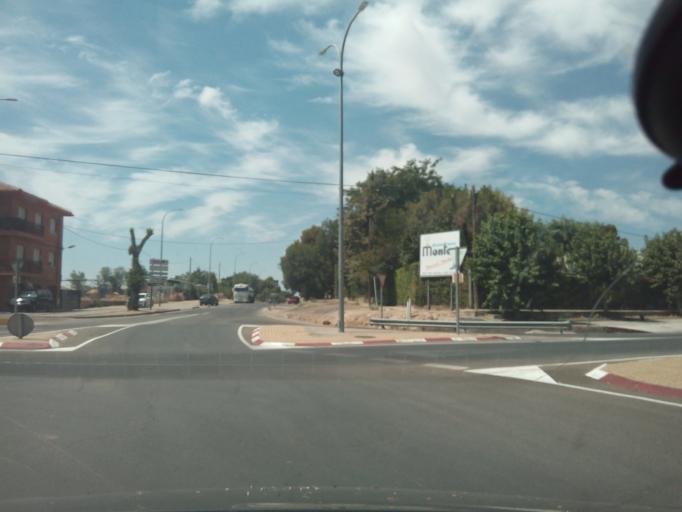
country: ES
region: Castille-La Mancha
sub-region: Province of Toledo
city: Villacanas
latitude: 39.6158
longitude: -3.3403
